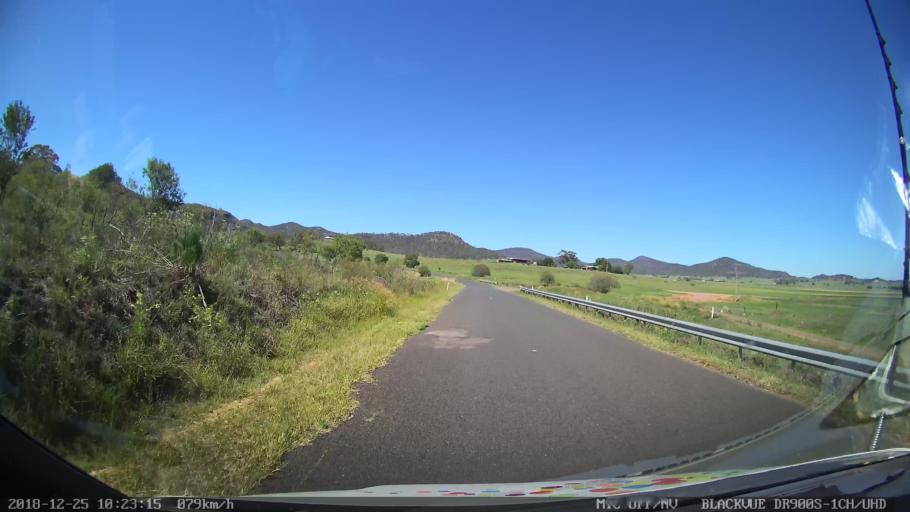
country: AU
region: New South Wales
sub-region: Muswellbrook
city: Denman
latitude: -32.3837
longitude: 150.5240
